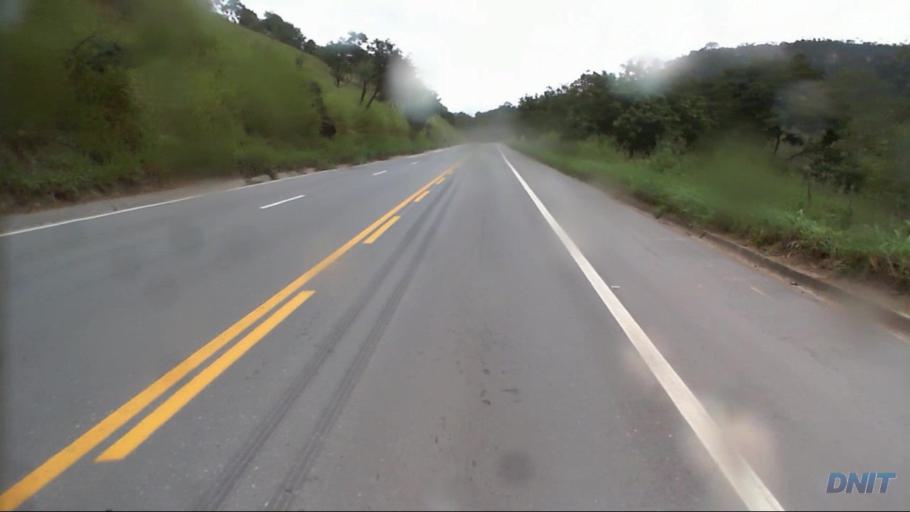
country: BR
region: Minas Gerais
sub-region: Nova Era
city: Nova Era
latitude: -19.7056
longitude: -42.9987
